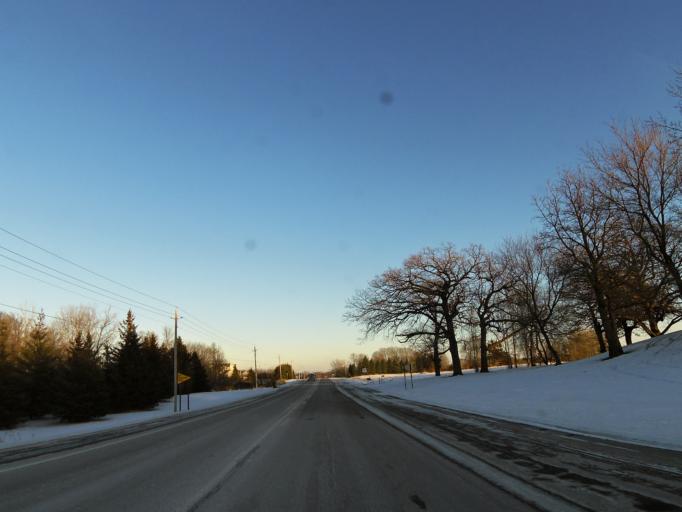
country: US
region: Minnesota
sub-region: Scott County
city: Shakopee
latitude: 44.7615
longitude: -93.5275
